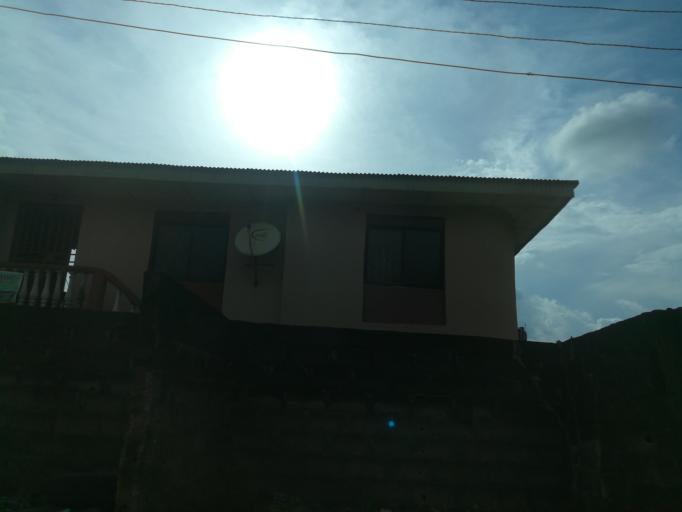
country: NG
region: Lagos
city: Ebute Ikorodu
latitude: 6.5969
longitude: 3.5053
